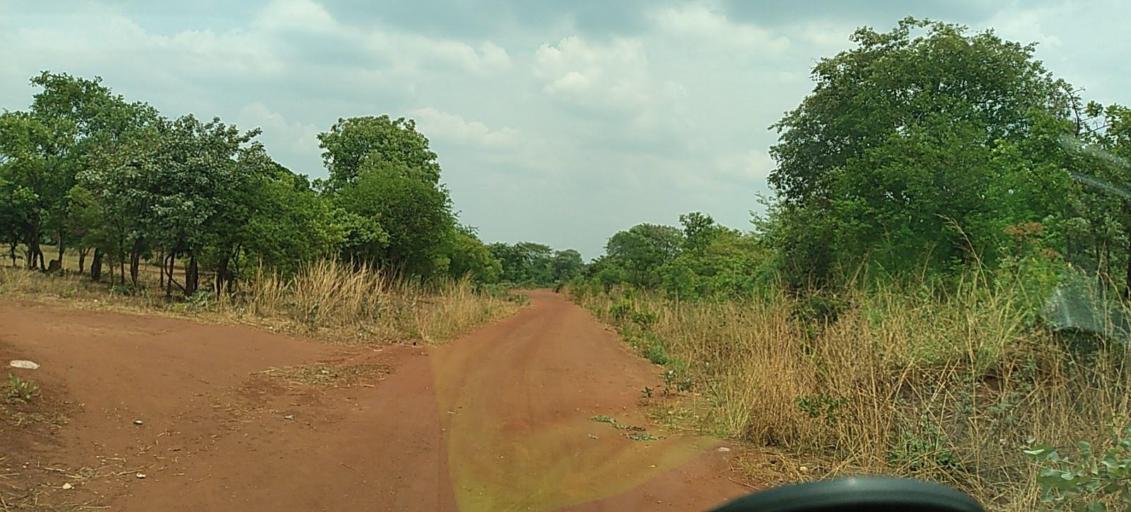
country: ZM
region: North-Western
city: Kansanshi
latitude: -12.0454
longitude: 26.3839
